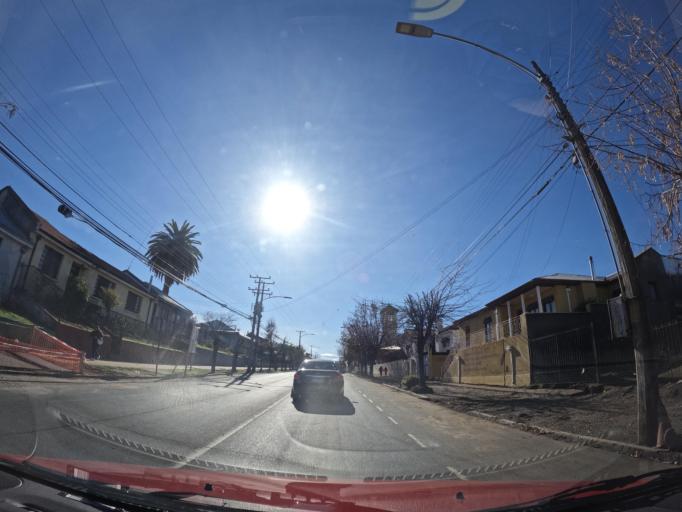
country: CL
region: Maule
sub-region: Provincia de Cauquenes
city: Cauquenes
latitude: -35.9711
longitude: -72.3148
